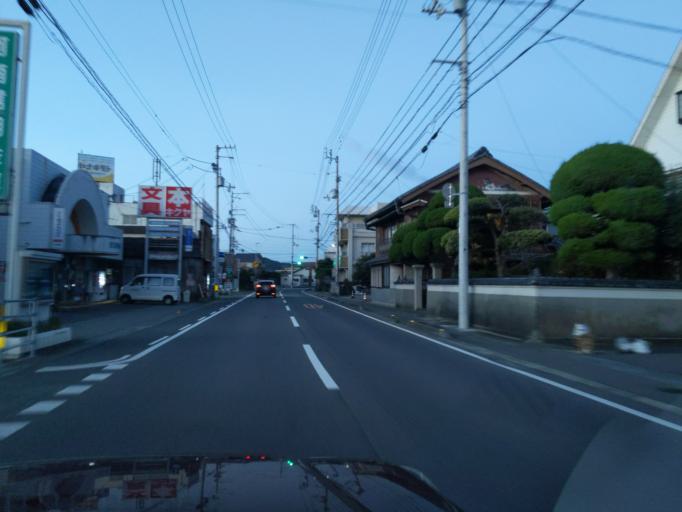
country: JP
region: Tokushima
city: Anan
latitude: 33.8734
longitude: 134.6429
